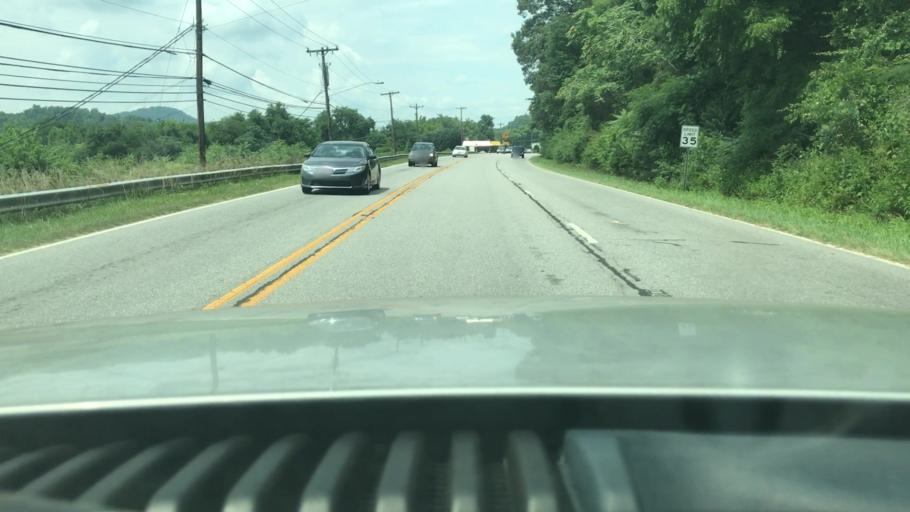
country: US
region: North Carolina
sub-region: Wilkes County
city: Wilkesboro
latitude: 36.1565
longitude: -81.1625
